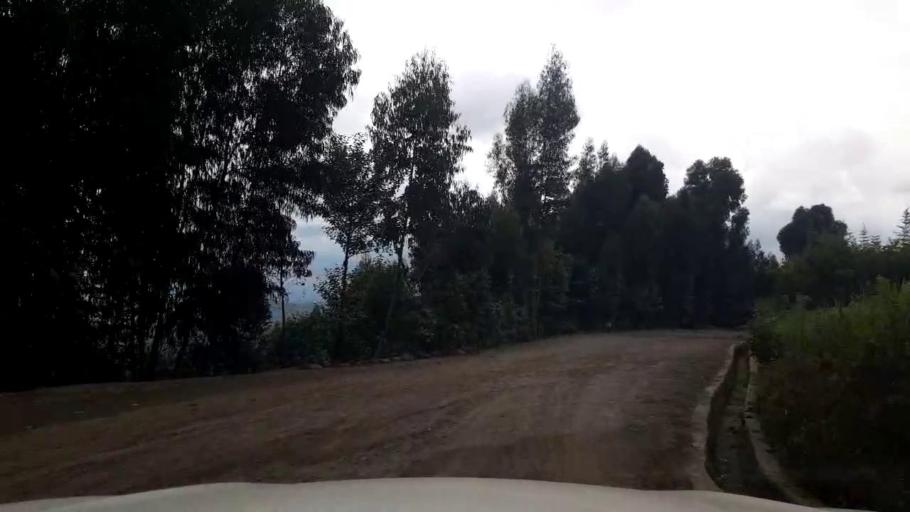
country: RW
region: Northern Province
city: Musanze
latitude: -1.5261
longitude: 29.5315
